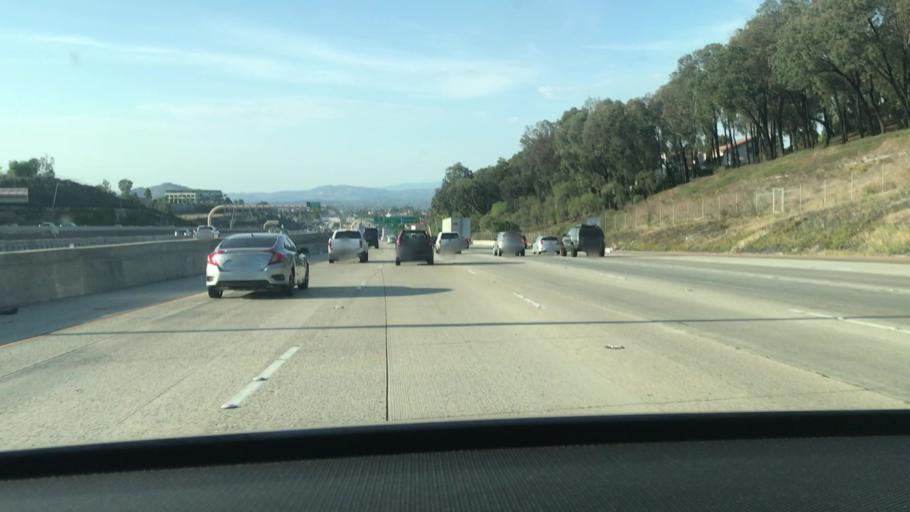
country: US
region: California
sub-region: San Diego County
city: Poway
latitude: 33.0062
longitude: -117.0803
